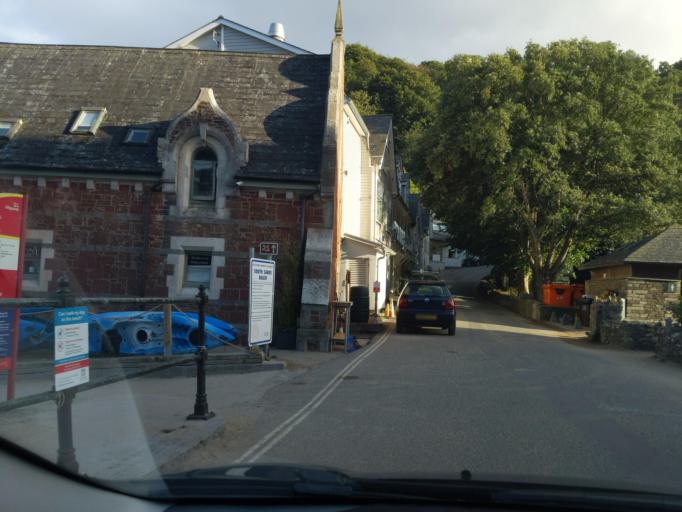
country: GB
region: England
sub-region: Devon
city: Salcombe
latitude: 50.2253
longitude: -3.7846
